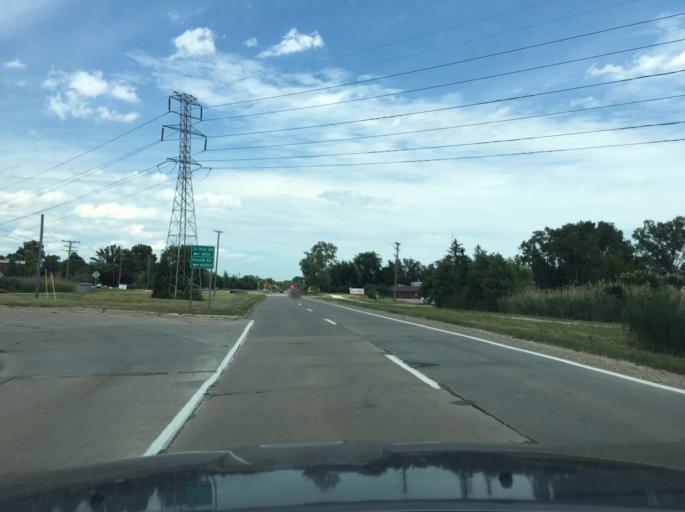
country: US
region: Michigan
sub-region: Macomb County
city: Shelby
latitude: 42.7130
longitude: -83.0539
